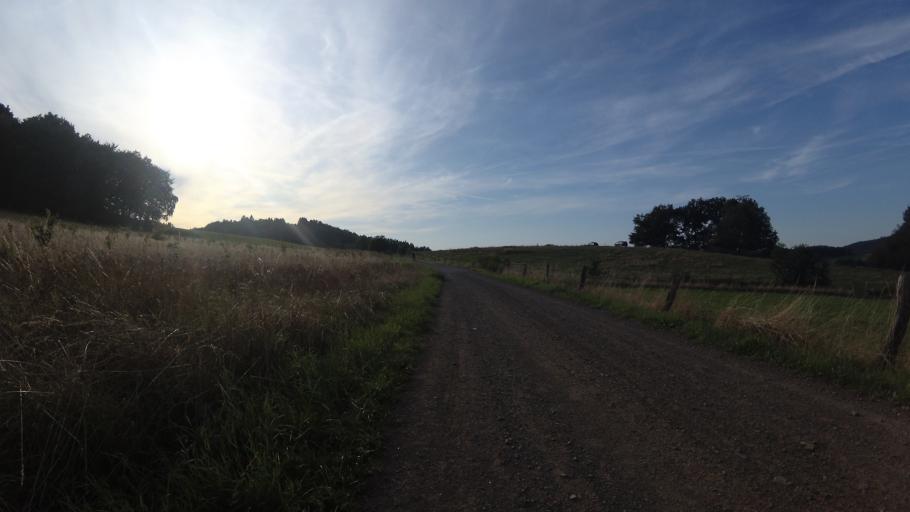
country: DE
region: Saarland
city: Namborn
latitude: 49.5421
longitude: 7.1280
